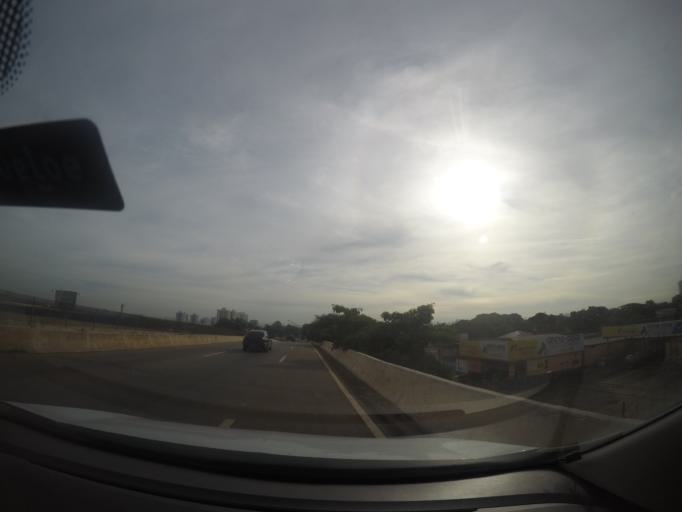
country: BR
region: Goias
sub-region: Goiania
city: Goiania
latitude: -16.7002
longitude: -49.3332
